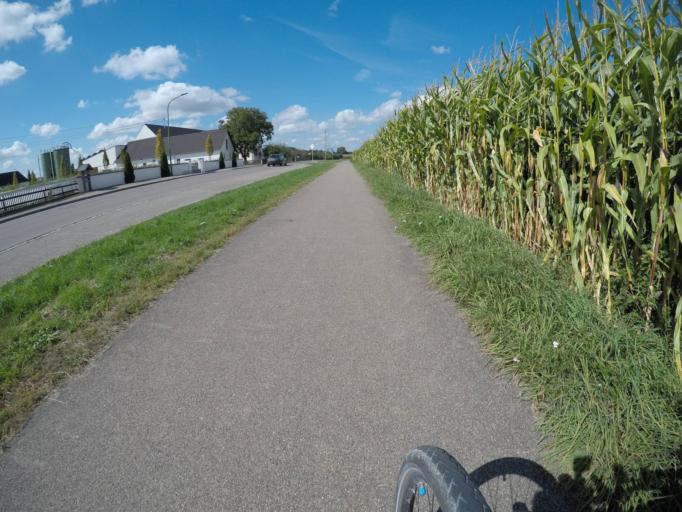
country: DE
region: Bavaria
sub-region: Swabia
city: Lutzingen
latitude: 48.6195
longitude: 10.5332
